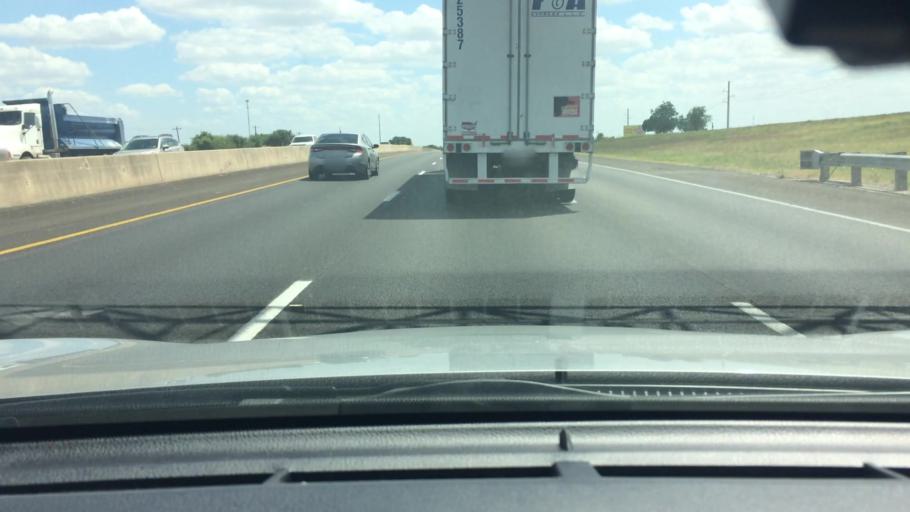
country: US
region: Texas
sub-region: Hays County
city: Kyle
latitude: 29.9752
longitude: -97.8745
